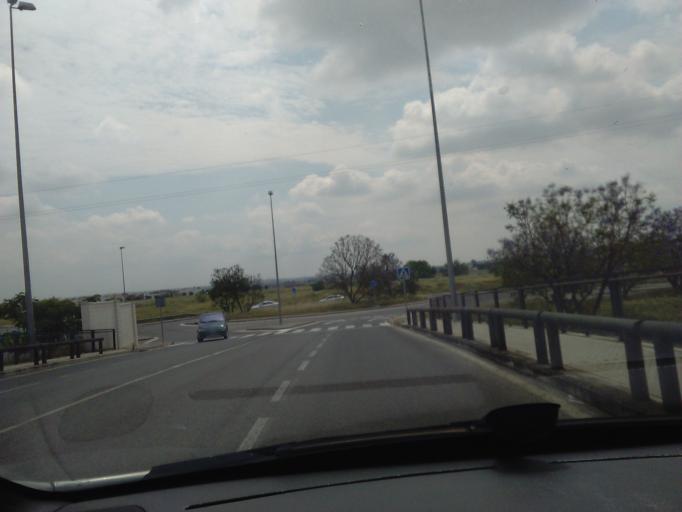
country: ES
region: Andalusia
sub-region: Provincia de Sevilla
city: Sevilla
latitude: 37.3716
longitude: -5.9388
